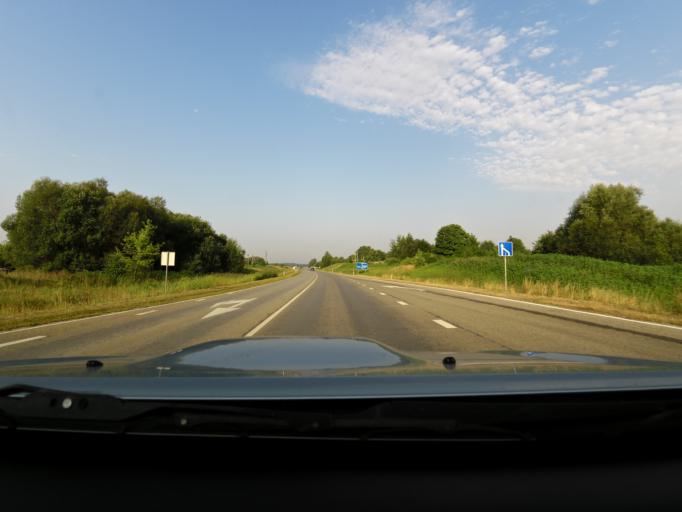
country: LT
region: Alytaus apskritis
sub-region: Alytaus rajonas
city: Daugai
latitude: 54.3691
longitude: 24.3515
